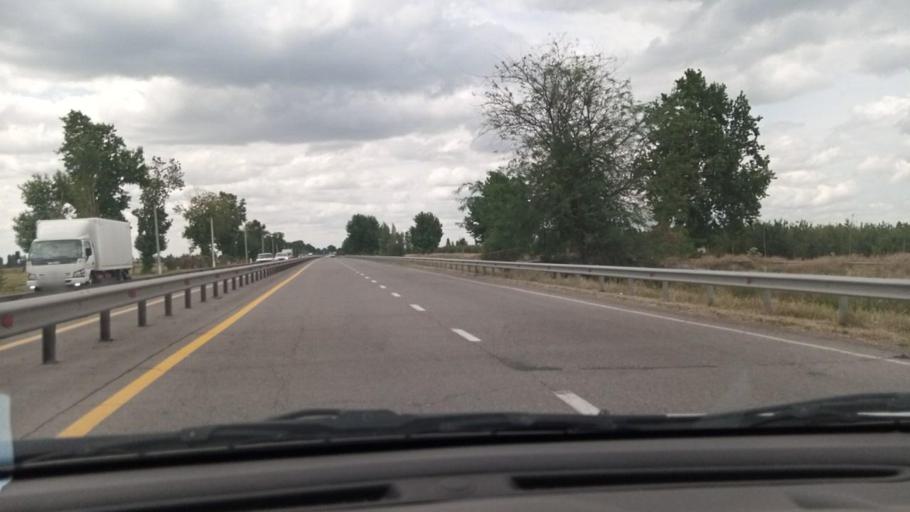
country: UZ
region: Toshkent Shahri
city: Bektemir
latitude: 41.1702
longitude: 69.4143
